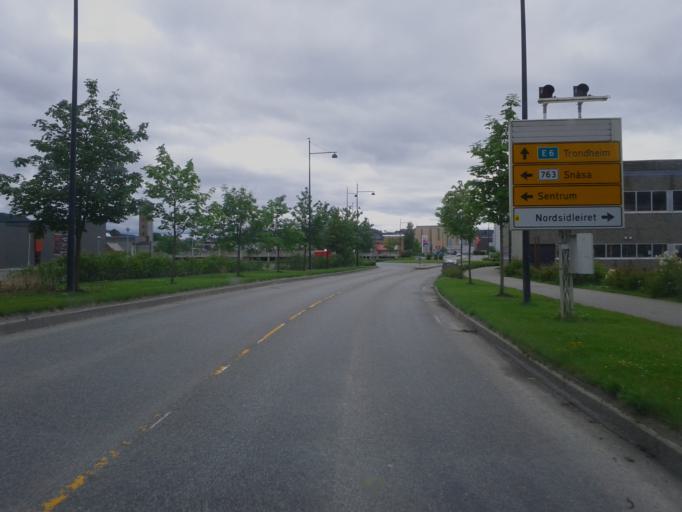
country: NO
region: Nord-Trondelag
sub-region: Steinkjer
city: Steinkjer
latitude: 64.0200
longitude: 11.4915
